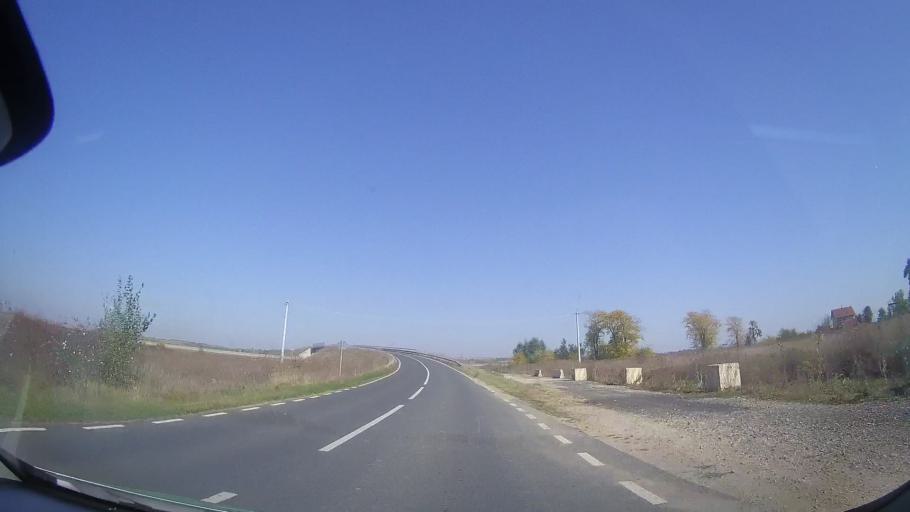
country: RO
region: Timis
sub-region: Comuna Balint
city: Balint
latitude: 45.7957
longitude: 21.8607
